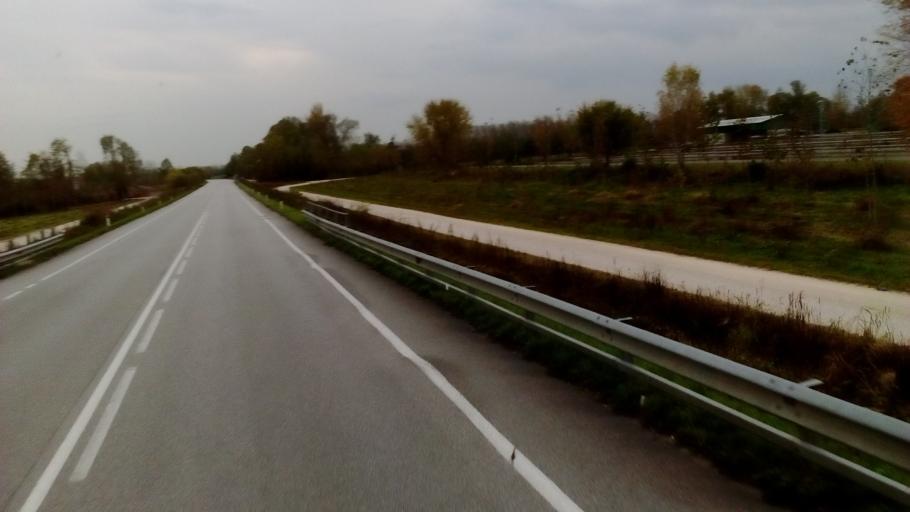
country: IT
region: Friuli Venezia Giulia
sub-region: Provincia di Pordenone
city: Orcenico Inferiore
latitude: 45.9642
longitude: 12.7385
